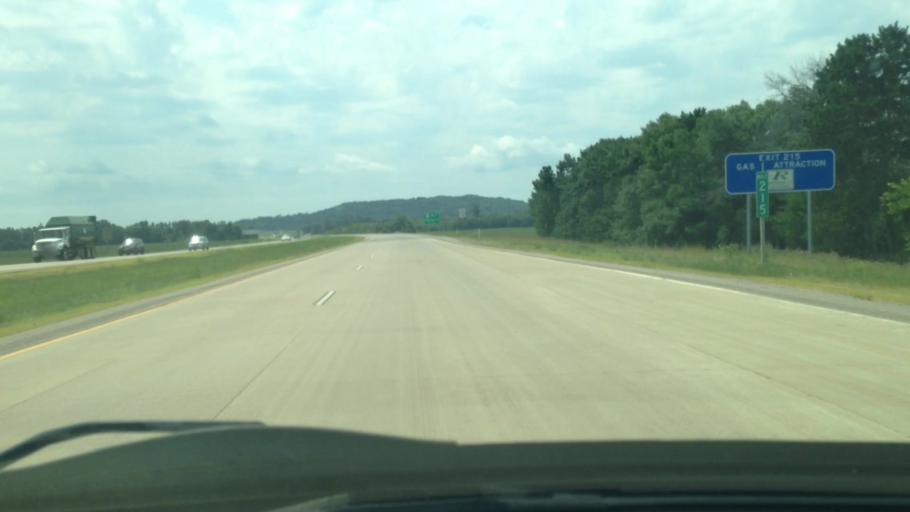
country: US
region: Wisconsin
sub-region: Sauk County
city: West Baraboo
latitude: 43.5262
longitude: -89.7878
